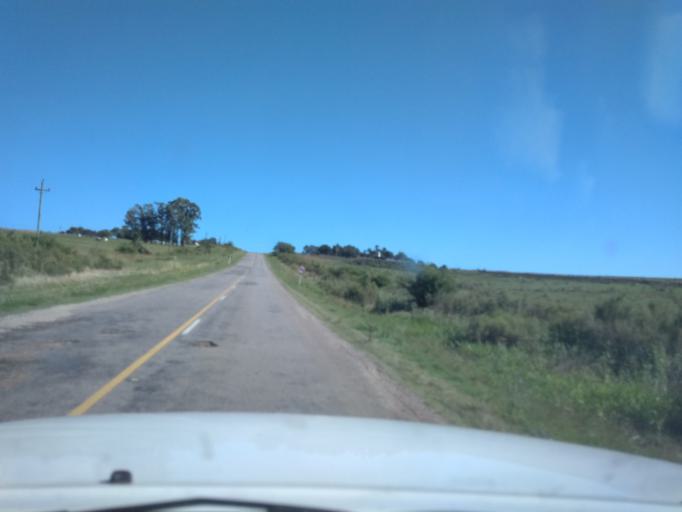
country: UY
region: Canelones
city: San Ramon
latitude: -34.1692
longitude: -55.9451
